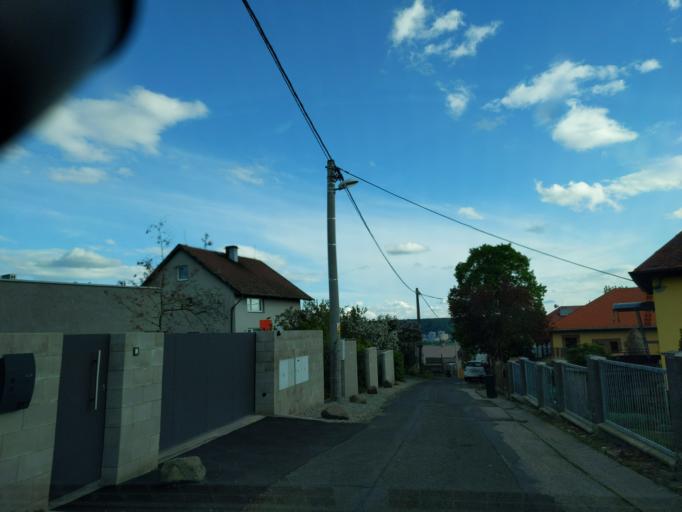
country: CZ
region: Ustecky
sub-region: Okres Usti nad Labem
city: Usti nad Labem
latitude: 50.7062
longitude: 14.0018
